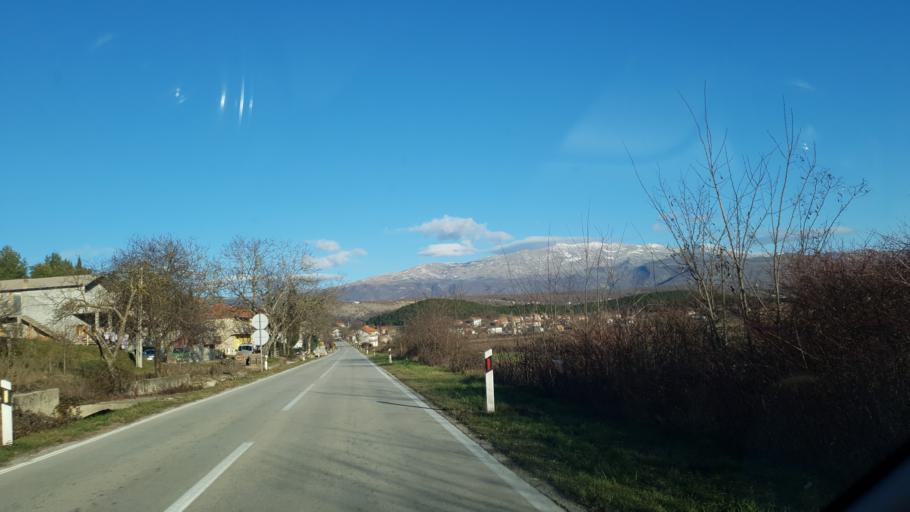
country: HR
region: Splitsko-Dalmatinska
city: Sinj
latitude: 43.7243
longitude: 16.6799
